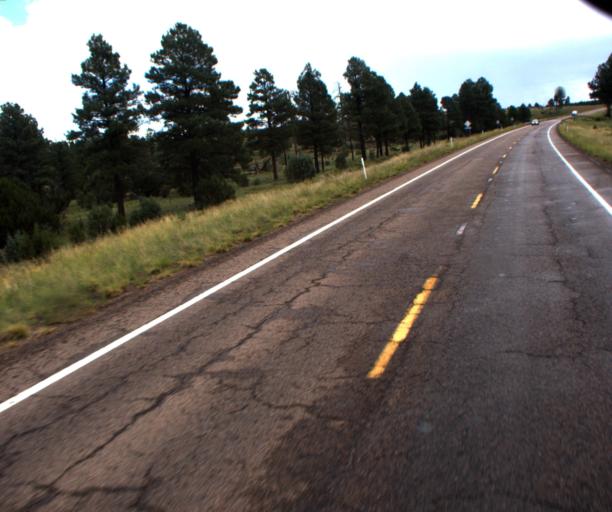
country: US
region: Arizona
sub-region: Navajo County
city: Heber-Overgaard
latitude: 34.3936
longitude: -110.5202
